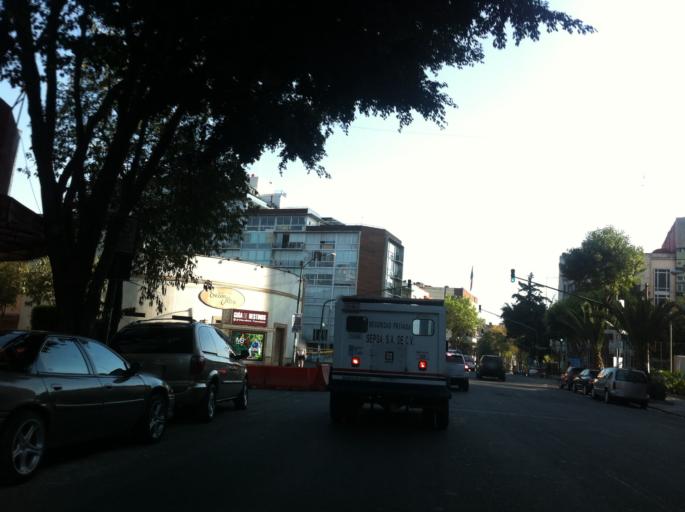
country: MX
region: Mexico City
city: Cuauhtemoc
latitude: 19.4247
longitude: -99.1615
